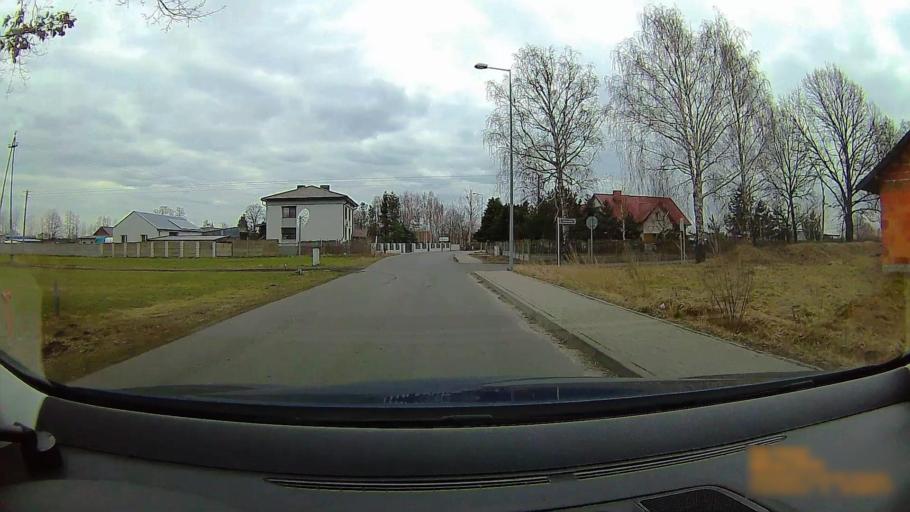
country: PL
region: Greater Poland Voivodeship
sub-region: Powiat koninski
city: Rychwal
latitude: 52.0761
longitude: 18.1465
